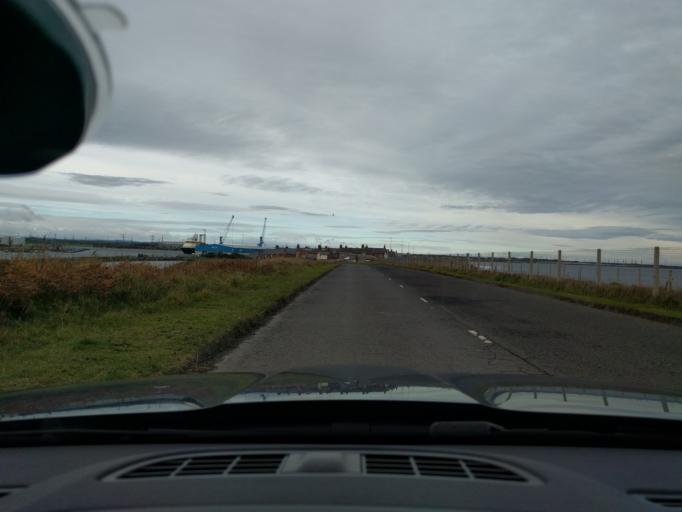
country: GB
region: England
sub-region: Northumberland
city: Blyth
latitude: 55.1332
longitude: -1.5063
